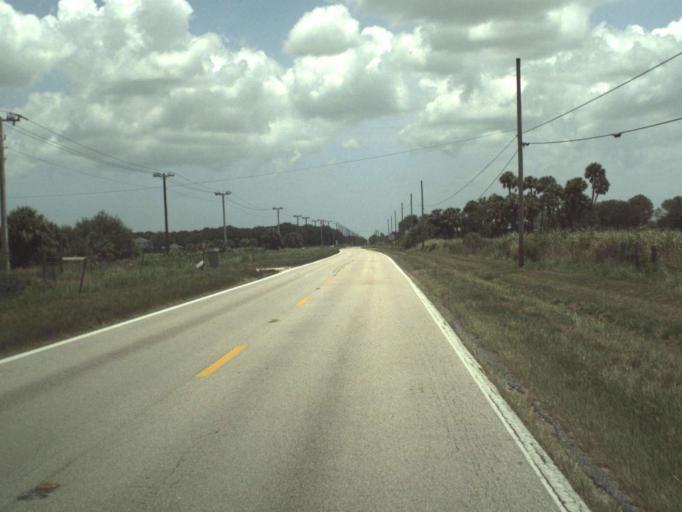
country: US
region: Florida
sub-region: Saint Lucie County
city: Fort Pierce South
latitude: 27.3744
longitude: -80.4530
